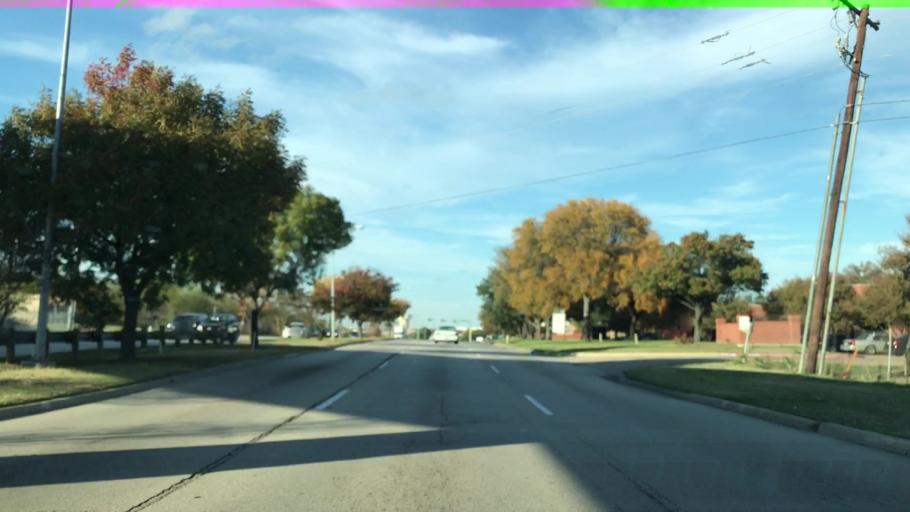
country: US
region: Texas
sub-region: Dallas County
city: Coppell
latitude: 32.8921
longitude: -96.9910
